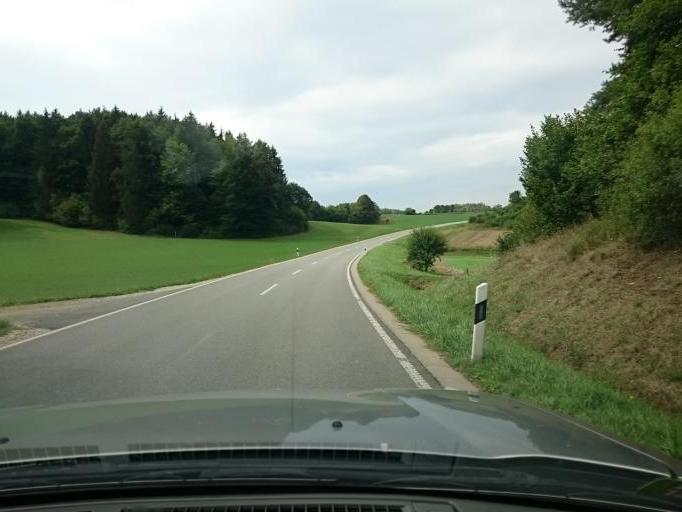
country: DE
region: Bavaria
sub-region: Regierungsbezirk Mittelfranken
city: Velden
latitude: 49.6470
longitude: 11.4803
